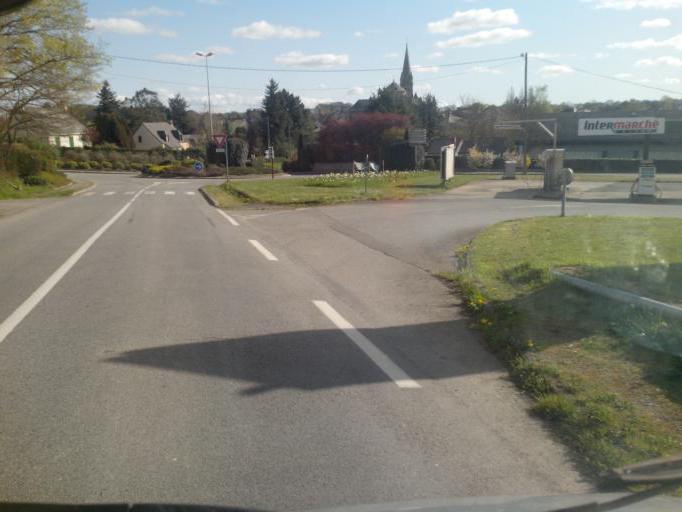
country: FR
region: Brittany
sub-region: Departement d'Ille-et-Vilaine
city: Maure-de-Bretagne
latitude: 47.8946
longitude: -1.9891
